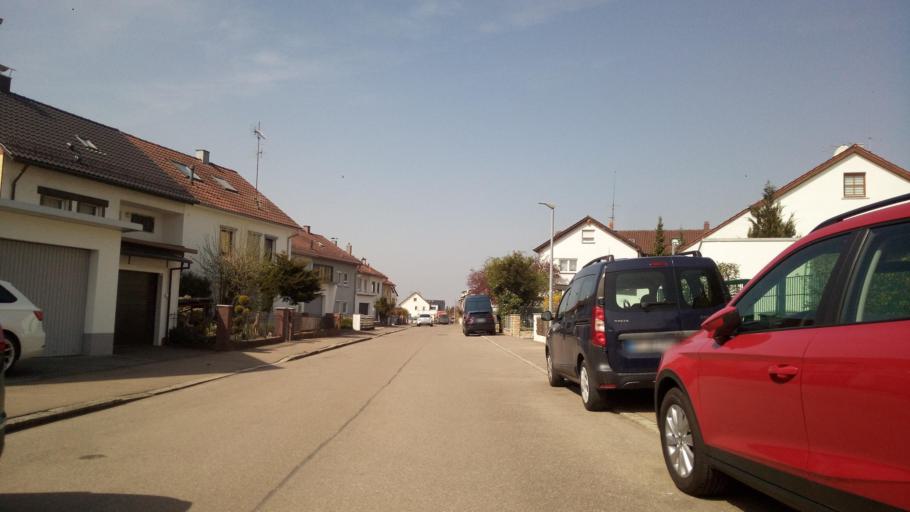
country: DE
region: Baden-Wuerttemberg
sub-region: Regierungsbezirk Stuttgart
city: Eislingen
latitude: 48.7034
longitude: 9.6839
